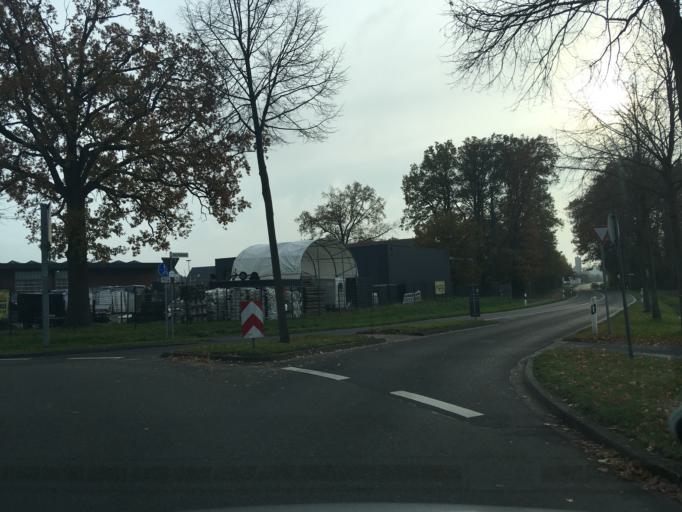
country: DE
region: North Rhine-Westphalia
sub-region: Regierungsbezirk Munster
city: Velen
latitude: 51.9010
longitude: 6.9764
